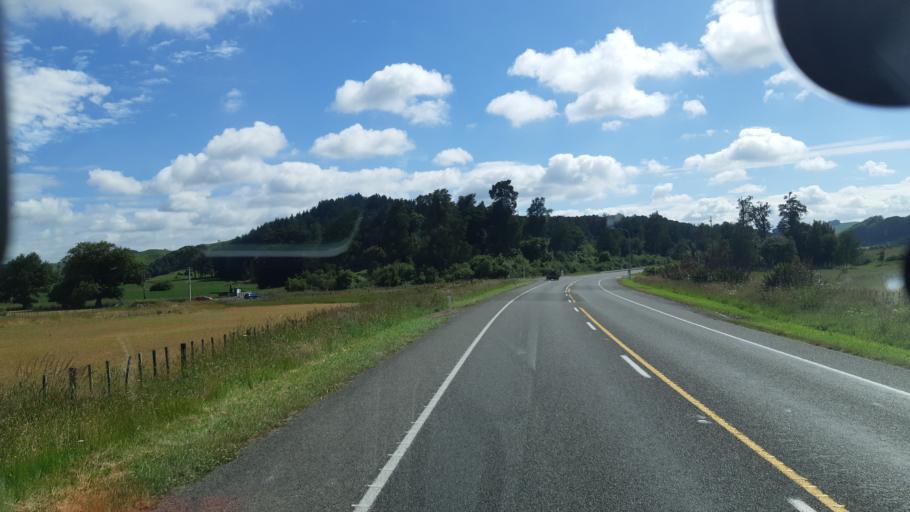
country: NZ
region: Manawatu-Wanganui
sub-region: Rangitikei District
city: Bulls
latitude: -39.9663
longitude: 175.5236
